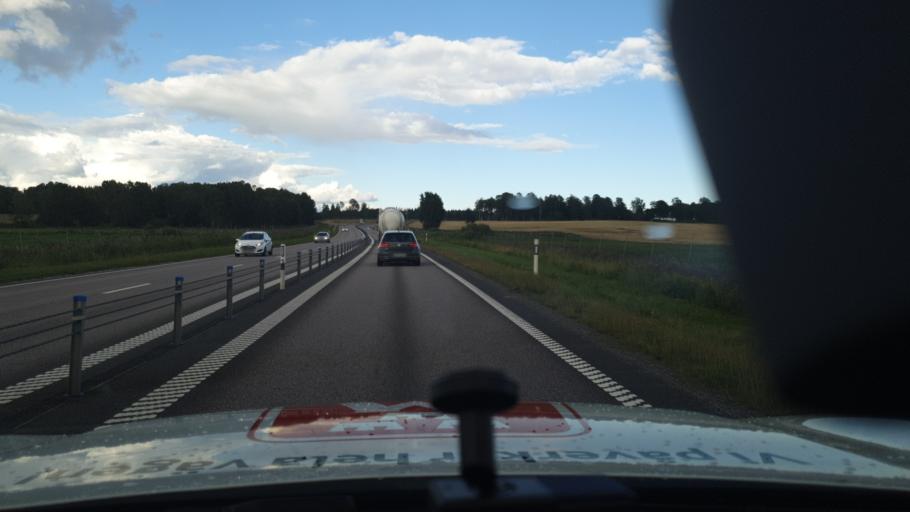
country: SE
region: Vaermland
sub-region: Karlstads Kommun
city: Edsvalla
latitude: 59.3899
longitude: 13.2660
